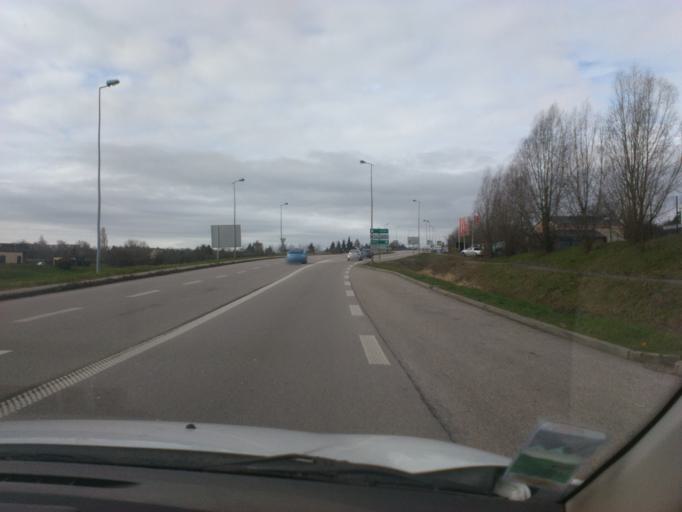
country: FR
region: Lorraine
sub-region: Departement des Vosges
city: Dogneville
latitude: 48.1988
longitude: 6.4767
